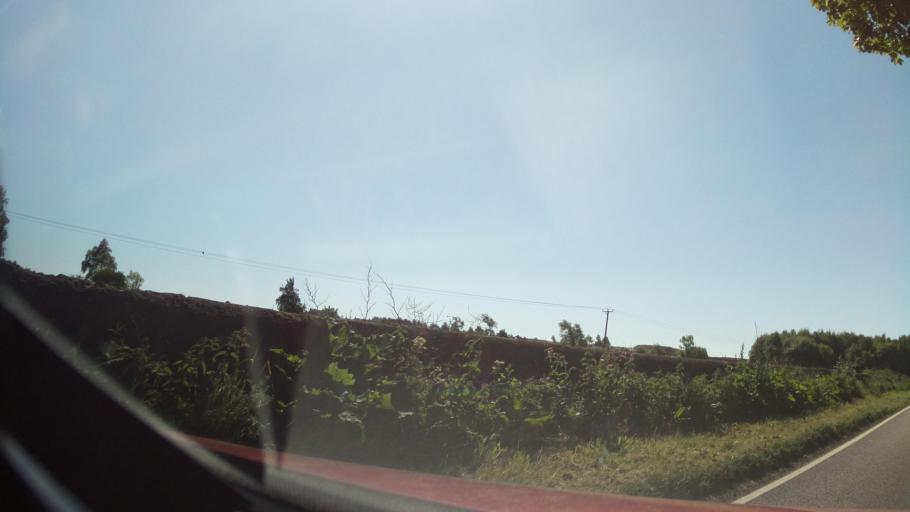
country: GB
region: Scotland
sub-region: Fife
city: Newport-On-Tay
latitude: 56.4183
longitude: -2.9180
